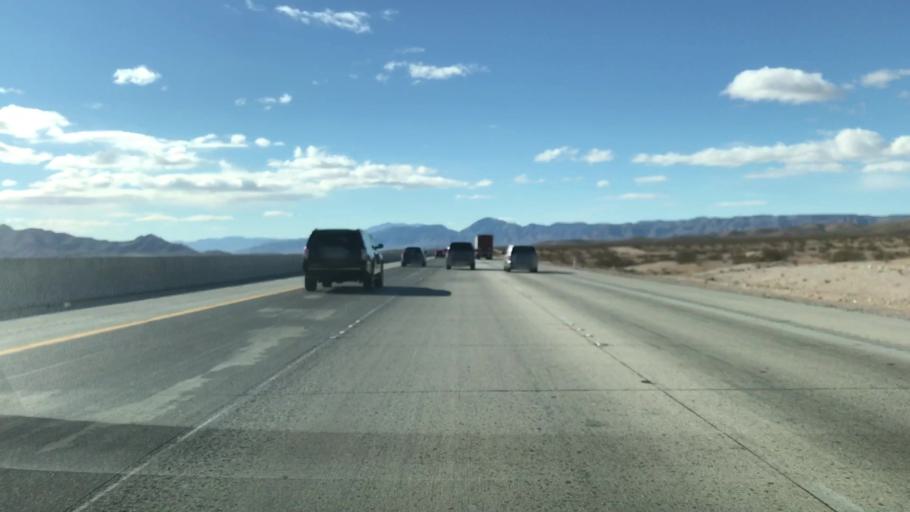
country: US
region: Nevada
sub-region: Clark County
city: Enterprise
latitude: 35.8523
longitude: -115.2646
